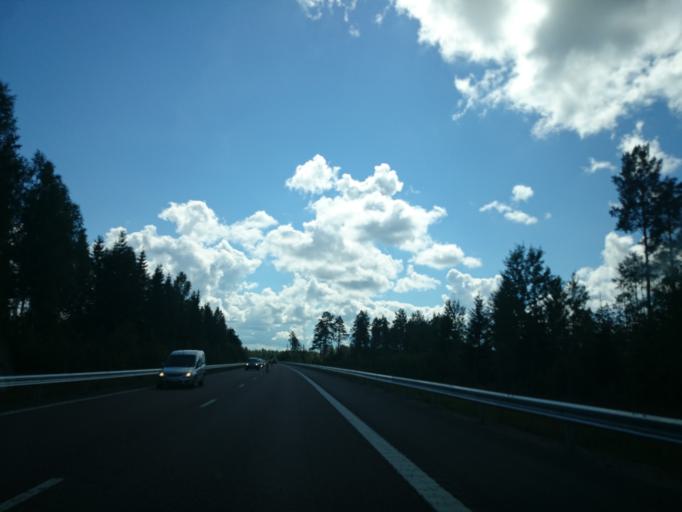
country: SE
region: Uppsala
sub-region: Alvkarleby Kommun
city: Skutskaer
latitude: 60.5267
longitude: 17.2724
